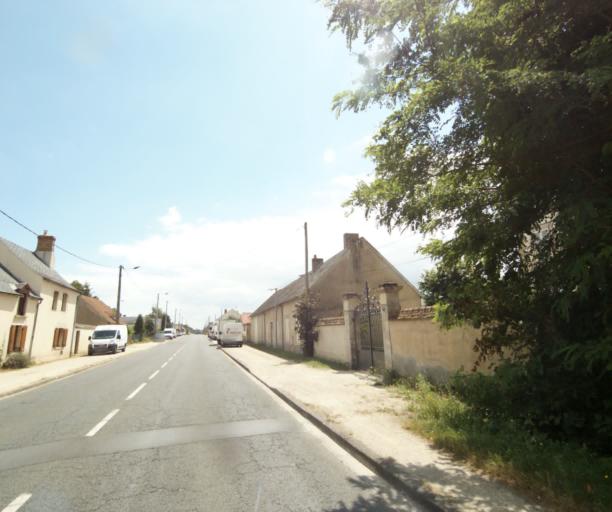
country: FR
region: Centre
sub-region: Departement du Loiret
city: Checy
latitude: 47.8989
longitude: 2.0171
